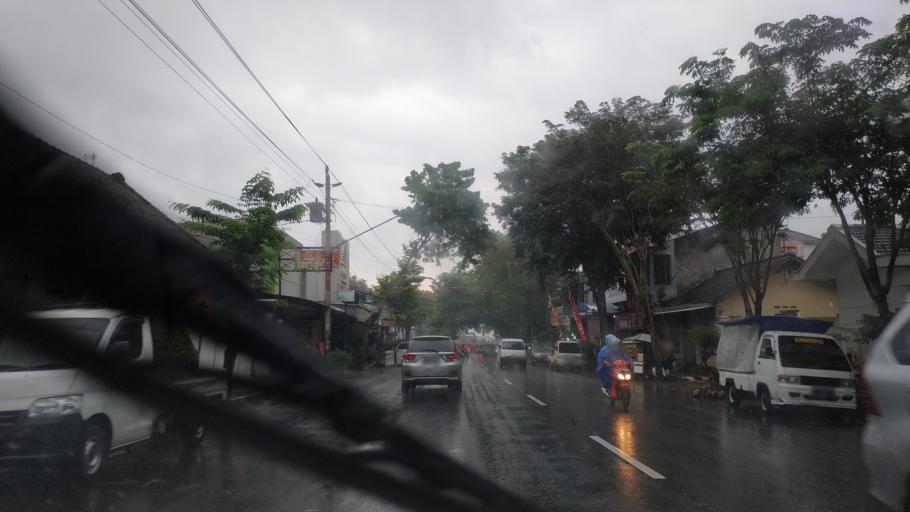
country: ID
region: Central Java
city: Magelang
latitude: -7.3159
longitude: 110.1735
